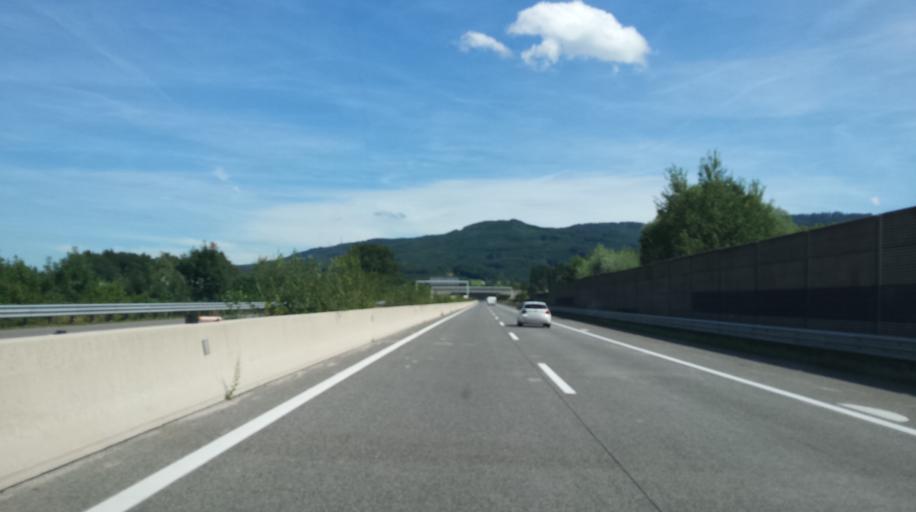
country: AT
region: Upper Austria
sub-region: Politischer Bezirk Vocklabruck
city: Aurach am Hongar
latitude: 47.9550
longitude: 13.6573
